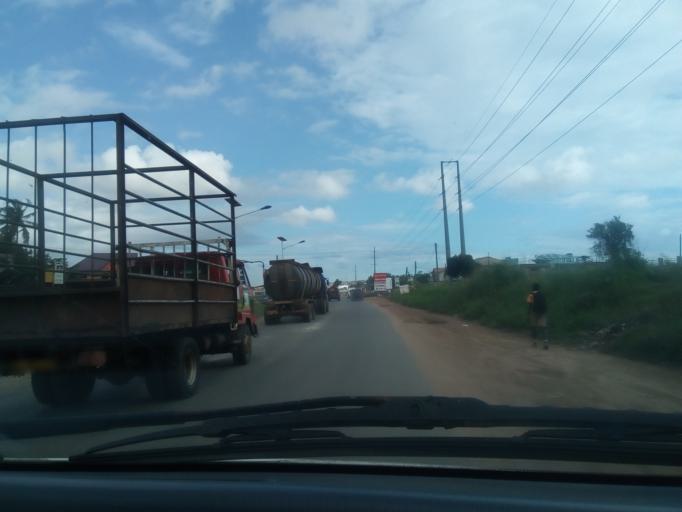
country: GH
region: Greater Accra
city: Achiaman
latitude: 5.7032
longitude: -0.2968
